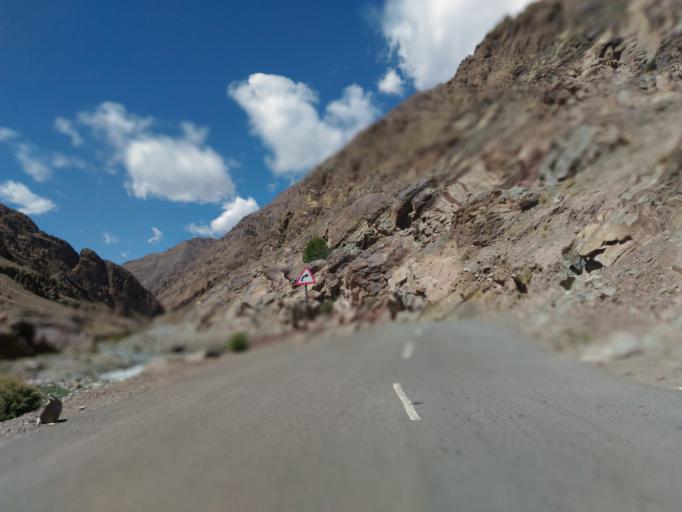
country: IN
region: Kashmir
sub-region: Ladakh
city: Leh
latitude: 33.8145
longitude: 77.8101
